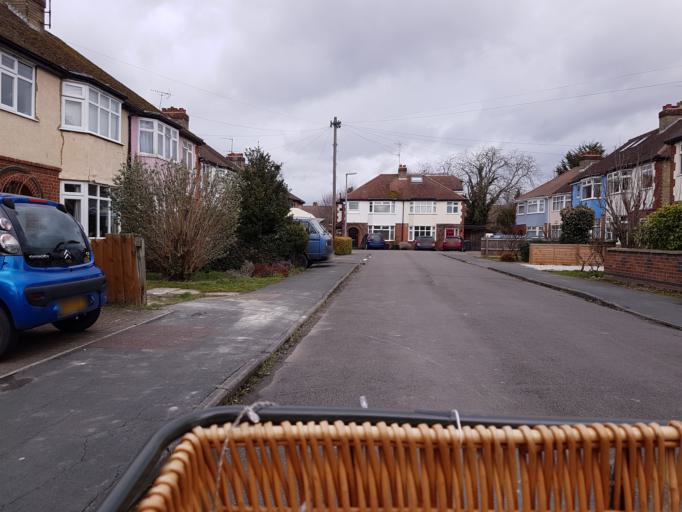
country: GB
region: England
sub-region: Cambridgeshire
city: Cambridge
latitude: 52.1874
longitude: 0.1571
